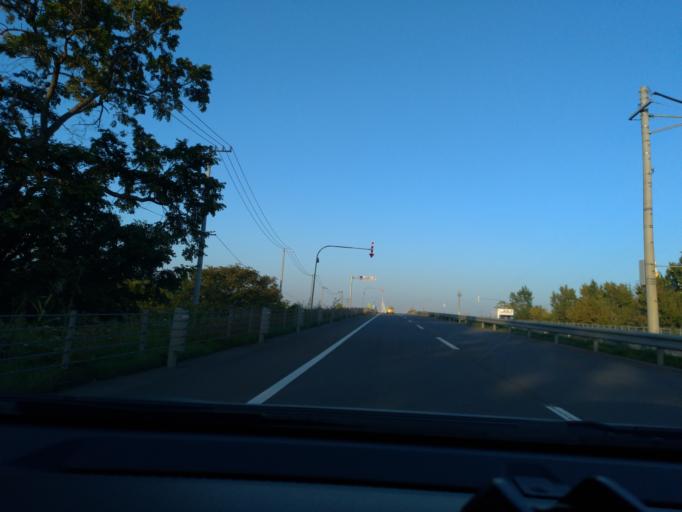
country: JP
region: Hokkaido
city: Ishikari
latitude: 43.1697
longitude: 141.4124
